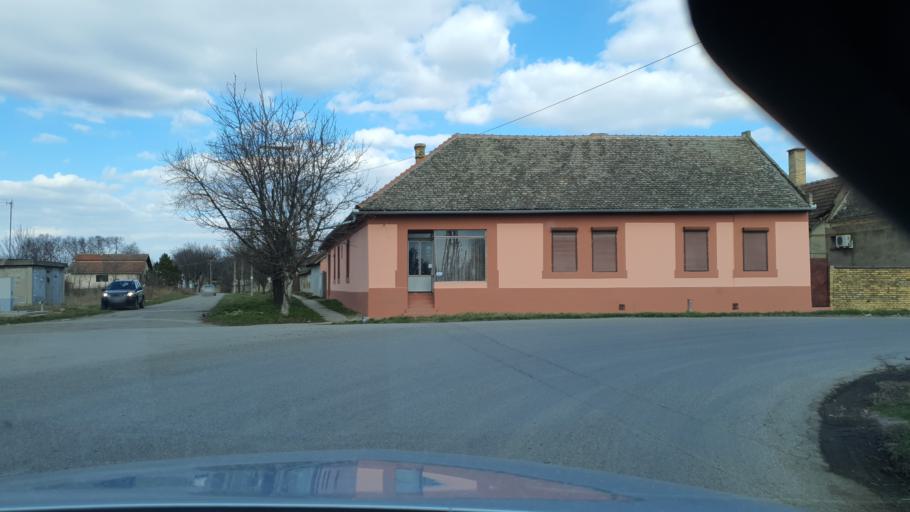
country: RS
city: Ravno Selo
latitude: 45.4532
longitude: 19.6155
